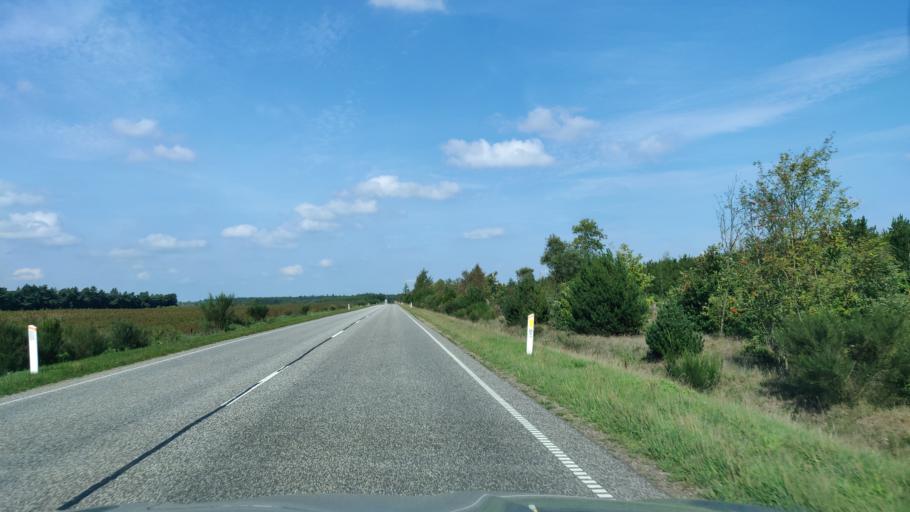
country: DK
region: Central Jutland
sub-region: Herning Kommune
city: Sunds
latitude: 56.3415
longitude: 8.9793
